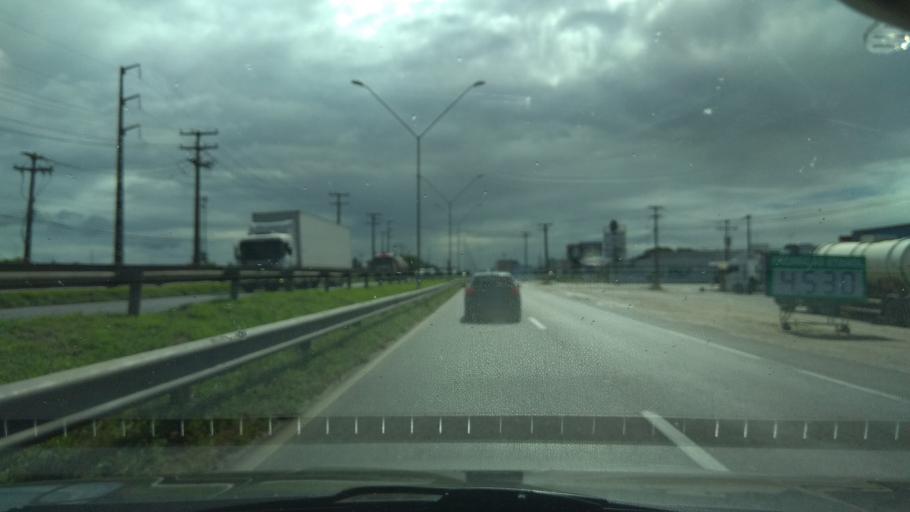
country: BR
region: Bahia
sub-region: Feira De Santana
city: Feira de Santana
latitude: -12.3114
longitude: -38.8847
